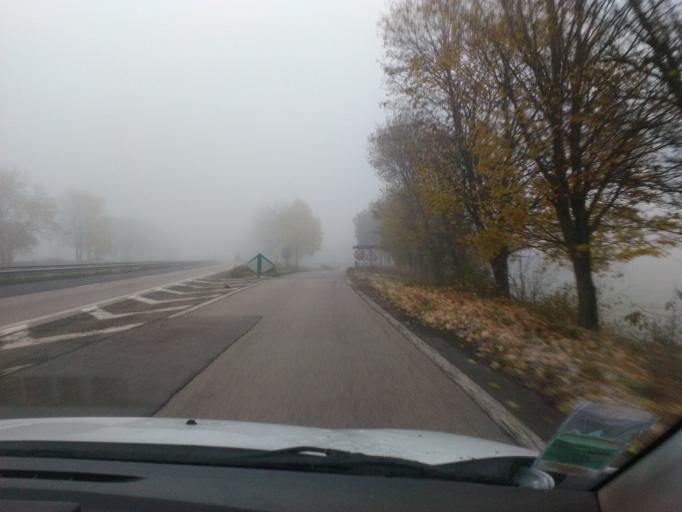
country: FR
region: Lorraine
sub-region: Departement des Vosges
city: Dogneville
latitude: 48.2130
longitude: 6.4562
